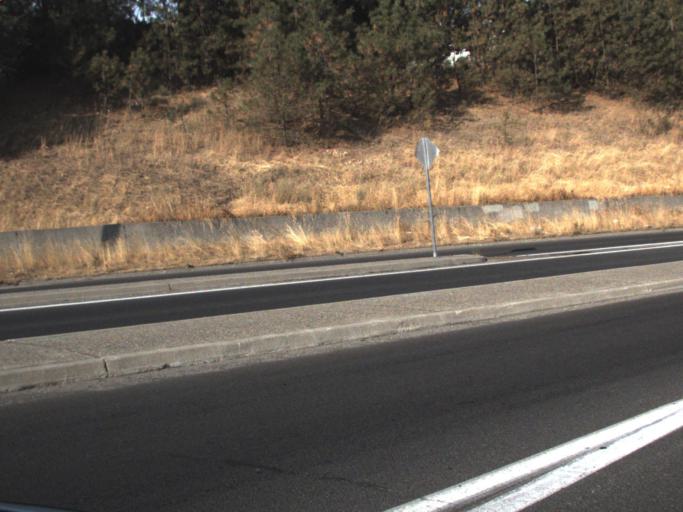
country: US
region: Washington
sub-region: Spokane County
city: Town and Country
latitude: 47.7155
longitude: -117.4776
